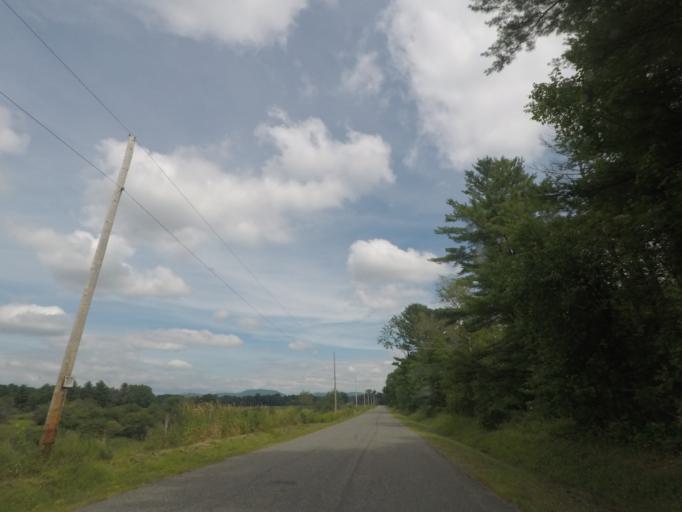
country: US
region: New York
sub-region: Saratoga County
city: Stillwater
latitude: 43.0109
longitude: -73.6350
